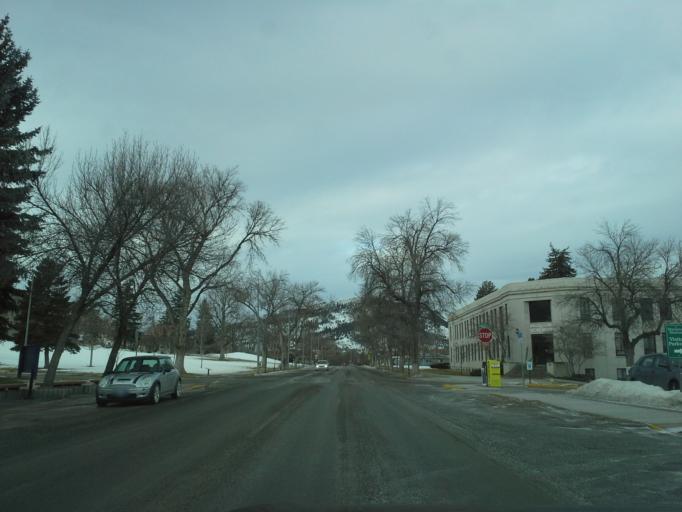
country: US
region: Montana
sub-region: Lewis and Clark County
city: Helena
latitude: 46.5868
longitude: -112.0159
